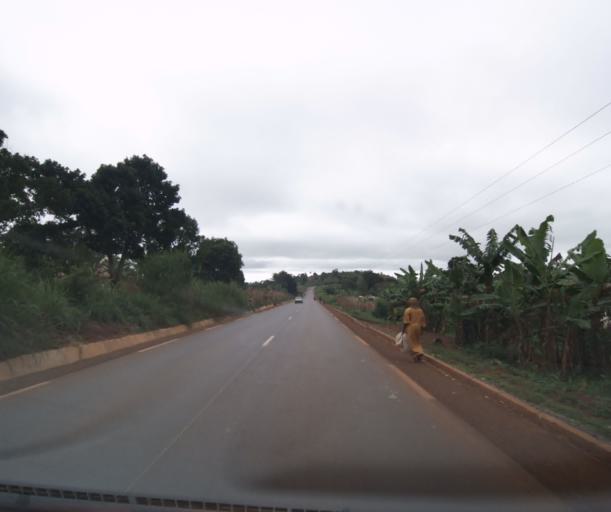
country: CM
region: West
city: Mbouda
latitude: 5.5541
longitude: 10.3217
